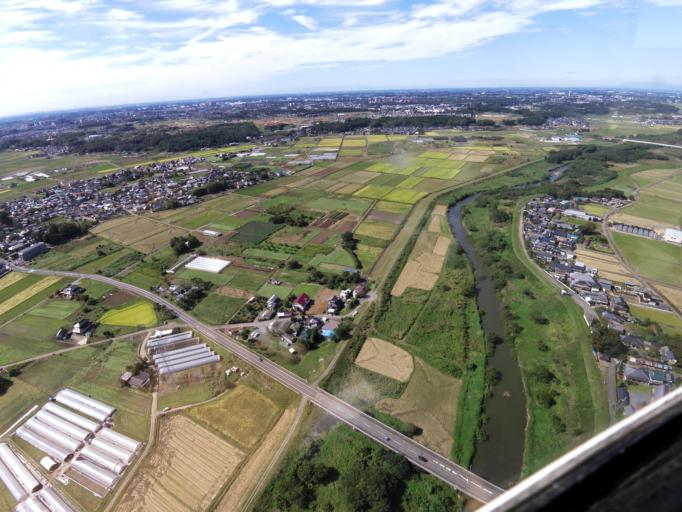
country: JP
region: Ibaraki
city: Naka
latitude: 36.1129
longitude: 140.1456
